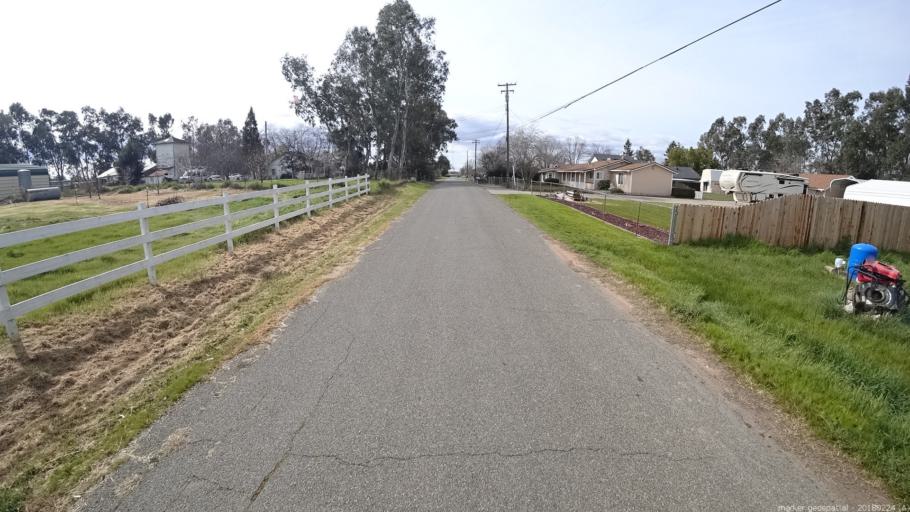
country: US
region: California
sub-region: Sacramento County
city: Elverta
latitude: 38.7077
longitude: -121.4547
